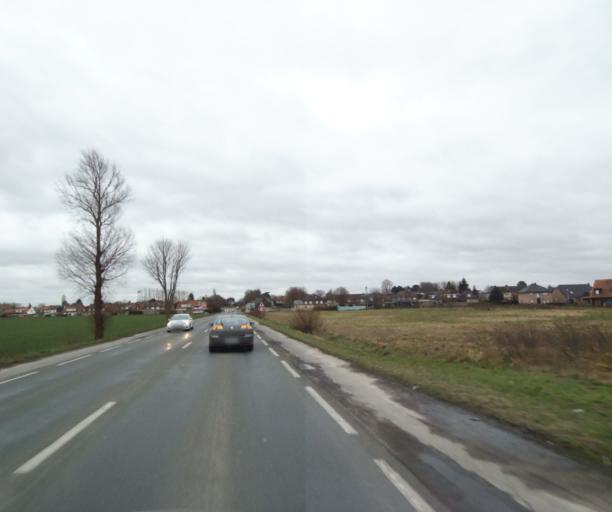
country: FR
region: Nord-Pas-de-Calais
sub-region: Departement du Nord
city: Saint-Saulve
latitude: 50.3777
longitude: 3.5650
